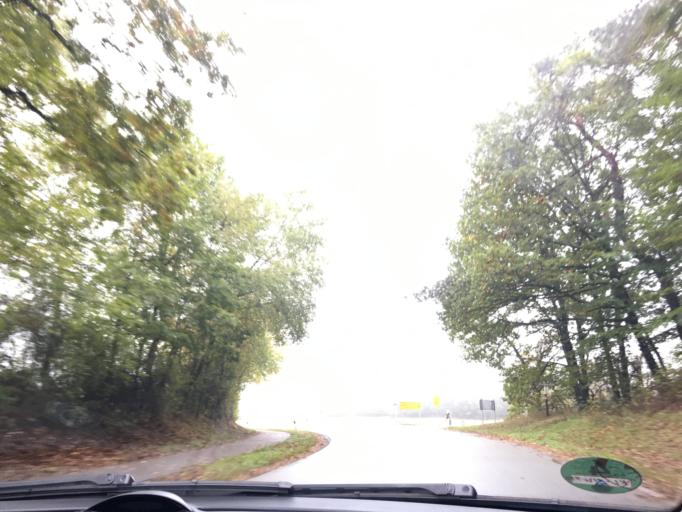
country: DE
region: Rheinland-Pfalz
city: Schmalenberg
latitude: 49.3285
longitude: 7.7463
